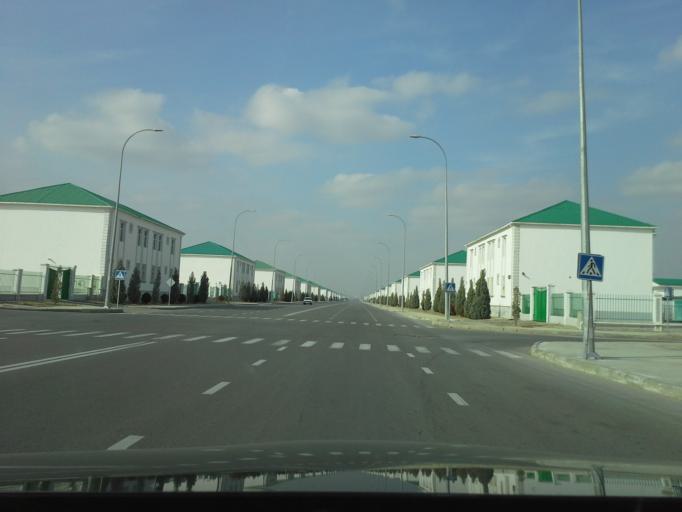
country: TM
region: Ahal
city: Abadan
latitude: 38.0775
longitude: 58.2805
